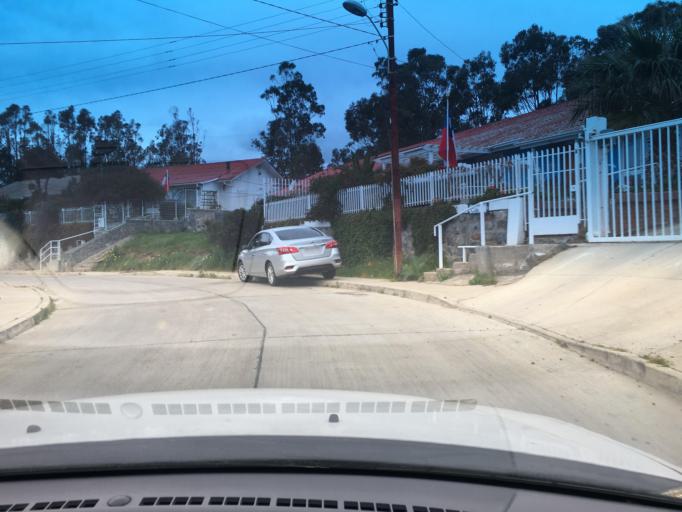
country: CL
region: Valparaiso
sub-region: Provincia de Valparaiso
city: Valparaiso
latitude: -33.1042
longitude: -71.6734
